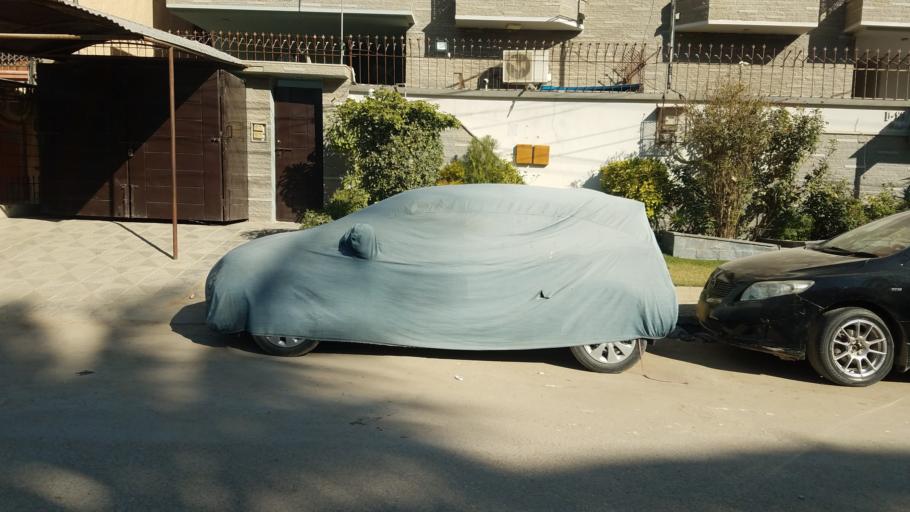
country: PK
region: Sindh
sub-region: Karachi District
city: Karachi
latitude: 24.9272
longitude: 67.0541
